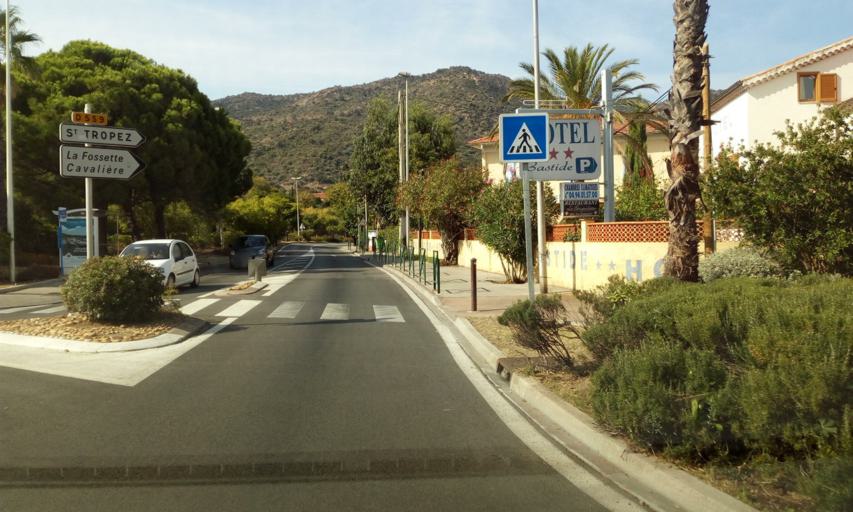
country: FR
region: Provence-Alpes-Cote d'Azur
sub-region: Departement du Var
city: Le Lavandou
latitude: 43.1411
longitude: 6.3798
